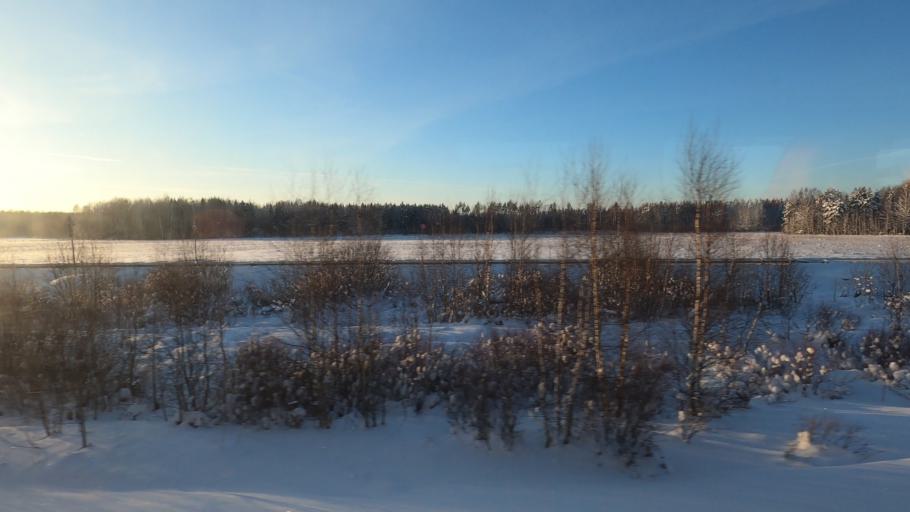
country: RU
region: Moskovskaya
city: Novo-Nikol'skoye
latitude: 56.6485
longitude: 37.5643
